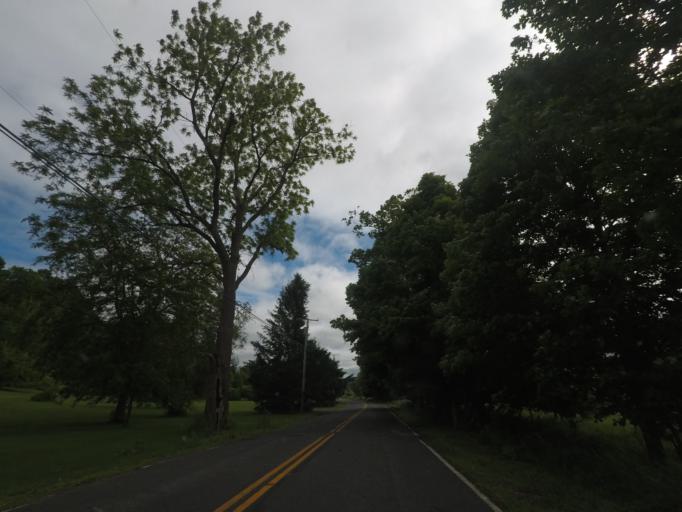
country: US
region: New York
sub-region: Dutchess County
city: Pine Plains
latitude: 42.0316
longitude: -73.5143
